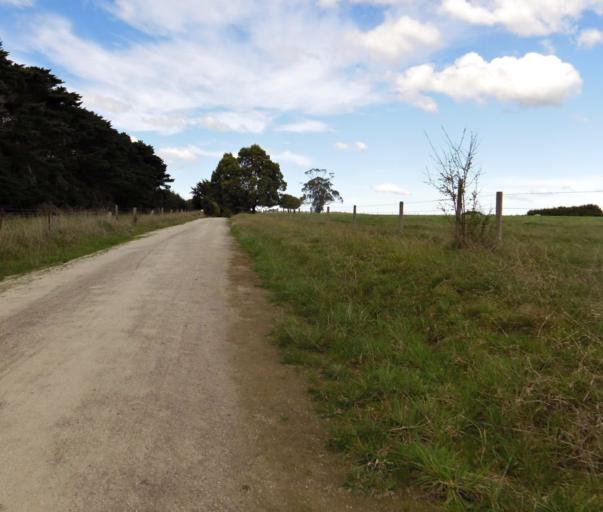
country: AU
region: Victoria
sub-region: Bass Coast
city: North Wonthaggi
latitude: -38.5261
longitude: 145.9450
